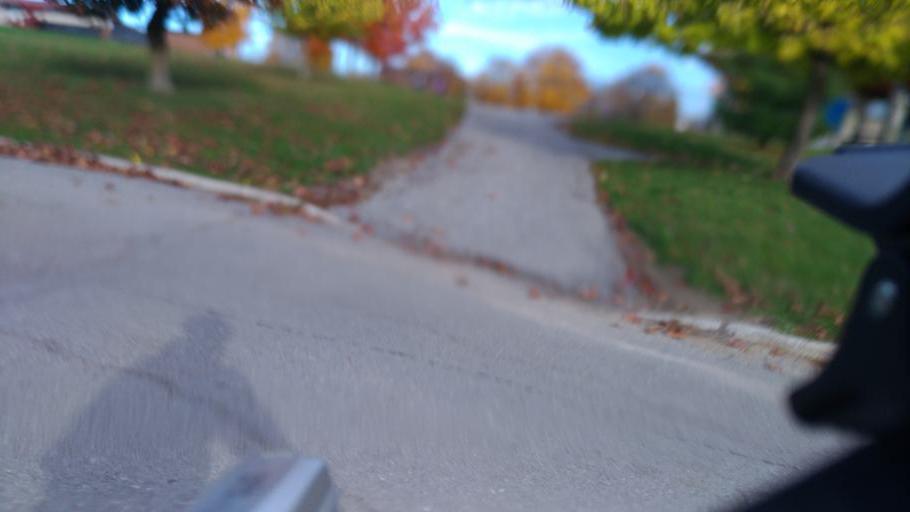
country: CA
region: Ontario
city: Bells Corners
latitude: 45.2953
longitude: -75.8856
